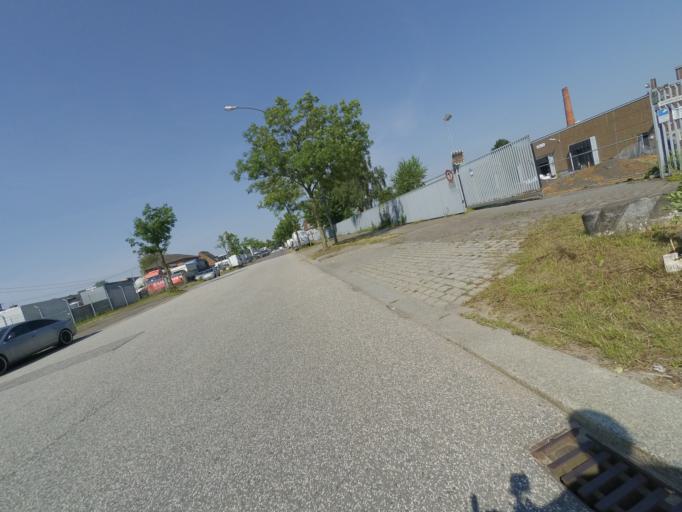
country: DE
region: Hamburg
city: Wandsbek
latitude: 53.5352
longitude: 10.1030
